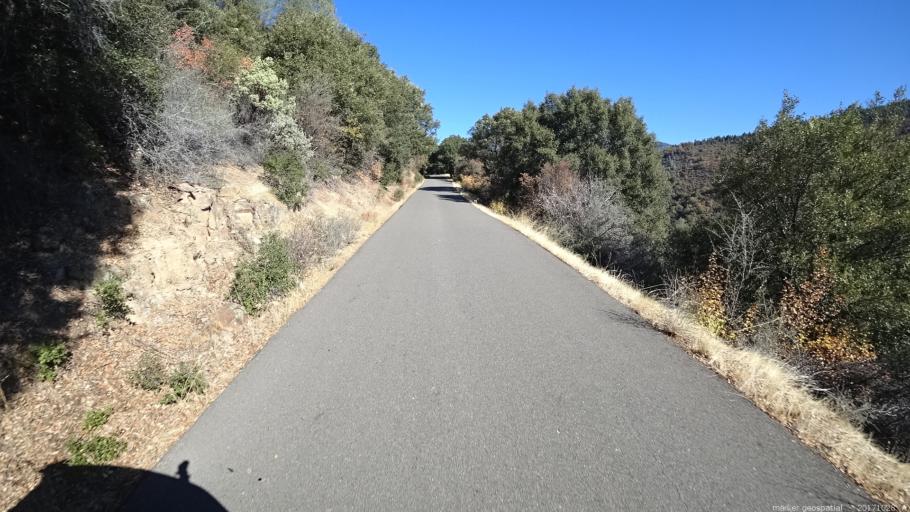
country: US
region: California
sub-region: Trinity County
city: Lewiston
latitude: 40.8039
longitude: -122.6110
